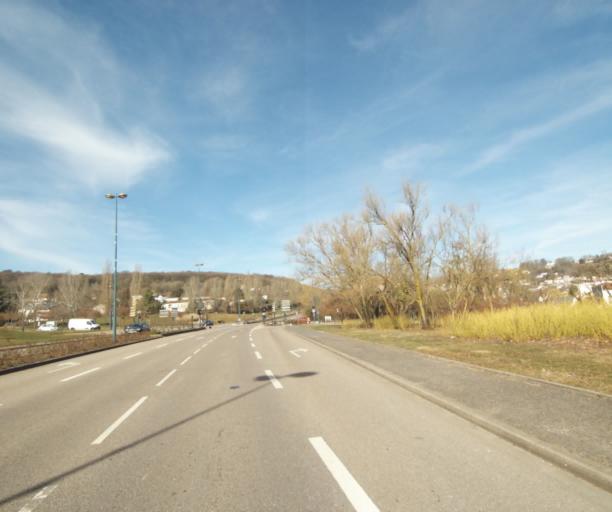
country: FR
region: Lorraine
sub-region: Departement de Meurthe-et-Moselle
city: Laxou
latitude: 48.6788
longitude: 6.1434
